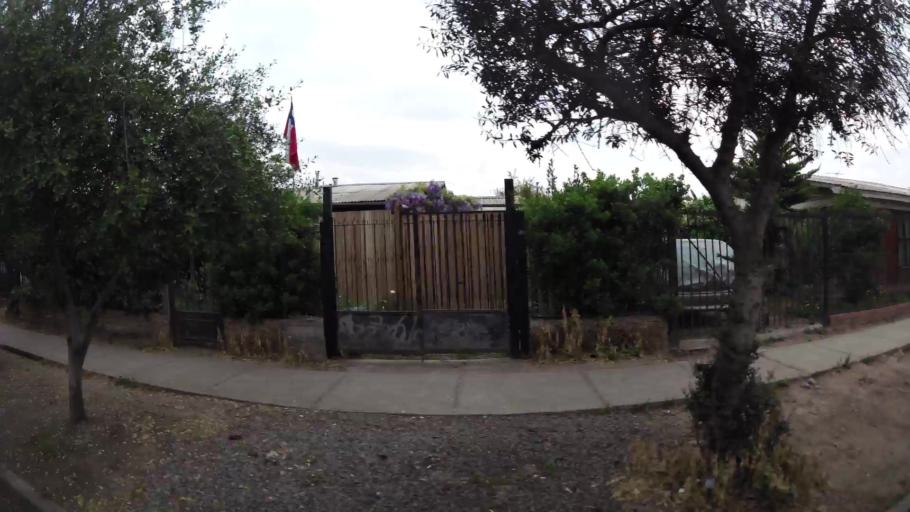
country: CL
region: Santiago Metropolitan
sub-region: Provincia de Chacabuco
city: Chicureo Abajo
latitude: -33.1999
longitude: -70.6752
